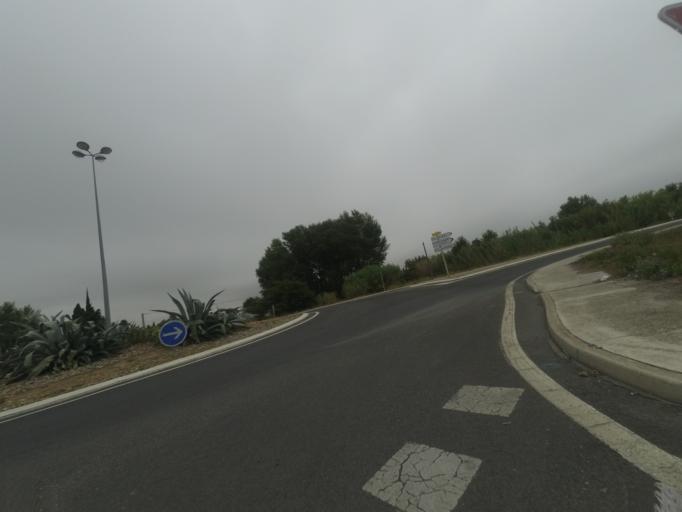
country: FR
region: Languedoc-Roussillon
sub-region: Departement des Pyrenees-Orientales
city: Baho
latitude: 42.6989
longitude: 2.8339
